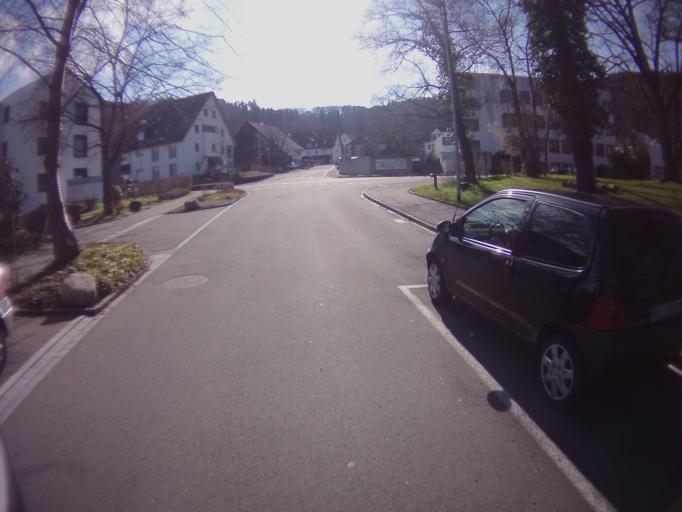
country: CH
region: Aargau
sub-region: Bezirk Baden
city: Spreitenbach
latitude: 47.4192
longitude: 8.3639
